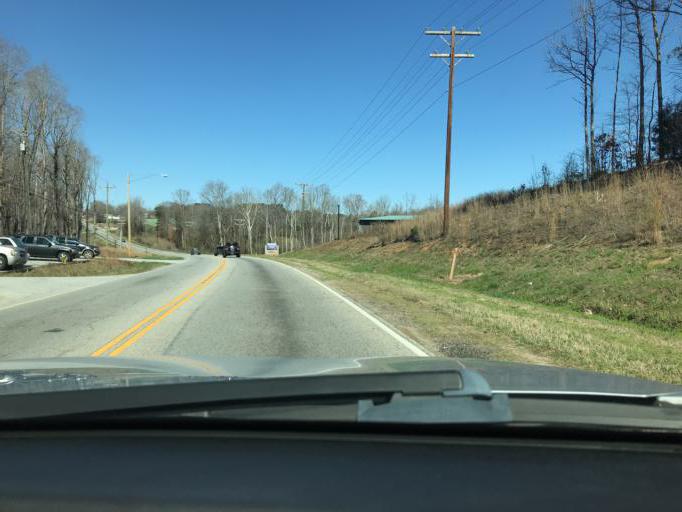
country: US
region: South Carolina
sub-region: Laurens County
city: Watts Mills
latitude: 34.4988
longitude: -81.9876
